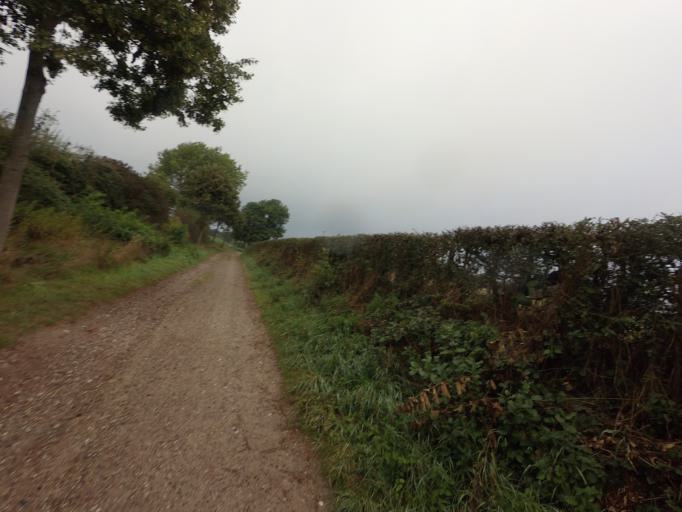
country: NL
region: Limburg
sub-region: Eijsden-Margraten
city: Margraten
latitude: 50.8226
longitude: 5.8084
